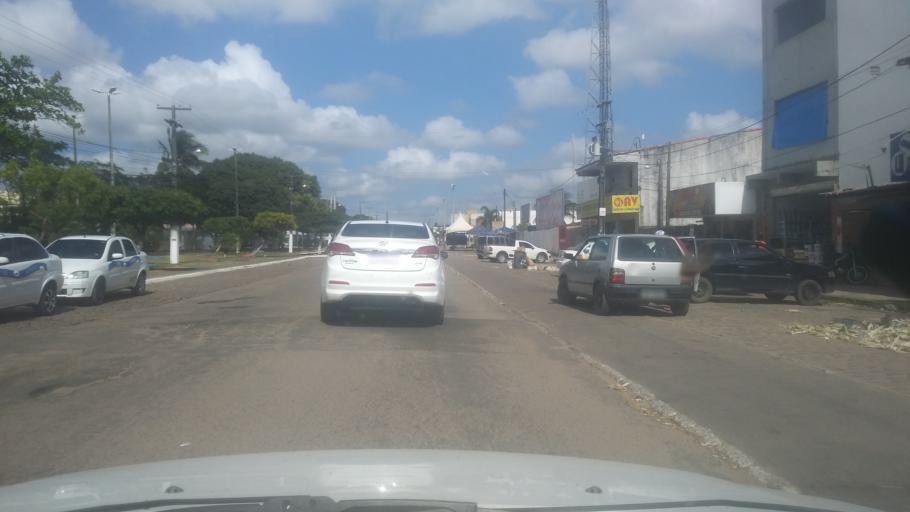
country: BR
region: Rio Grande do Norte
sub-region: Extremoz
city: Extremoz
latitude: -5.7042
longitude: -35.2916
